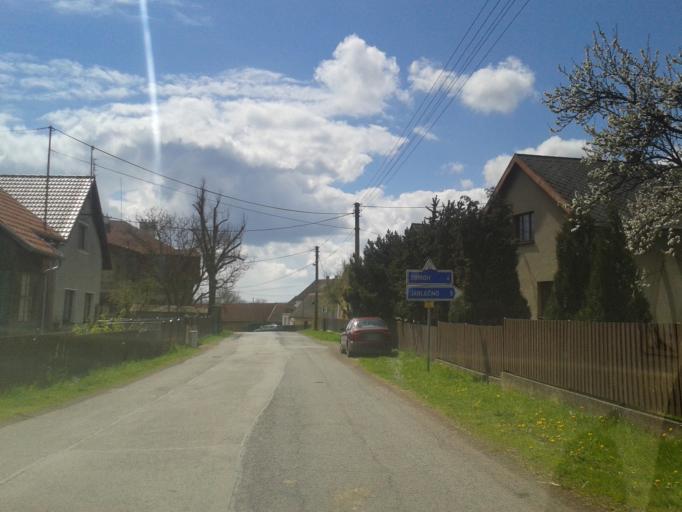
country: CZ
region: Plzensky
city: Zbiroh
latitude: 49.8870
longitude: 13.8042
